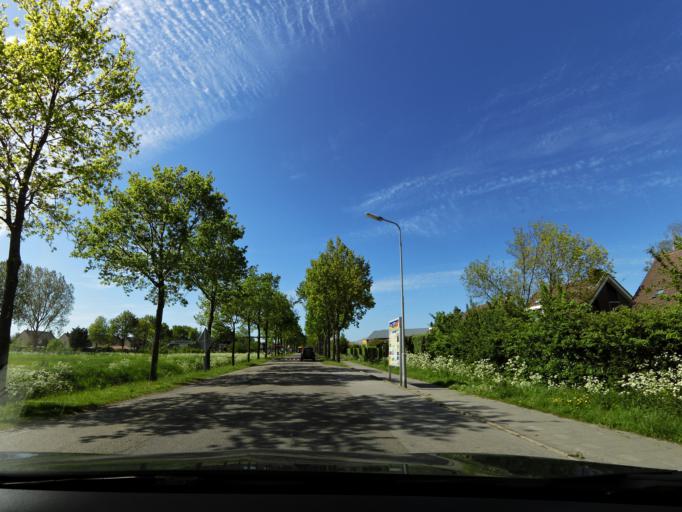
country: NL
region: Zeeland
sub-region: Schouwen-Duiveland
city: Bruinisse
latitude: 51.6466
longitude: 3.9991
